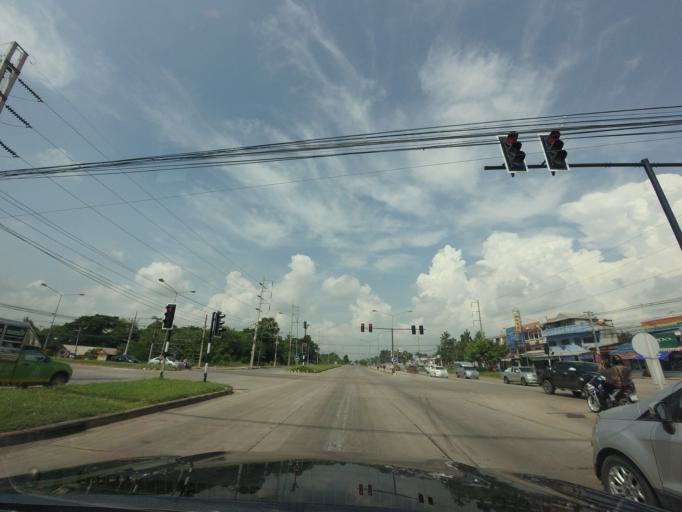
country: TH
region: Khon Kaen
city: Ban Fang
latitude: 16.4499
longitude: 102.7151
